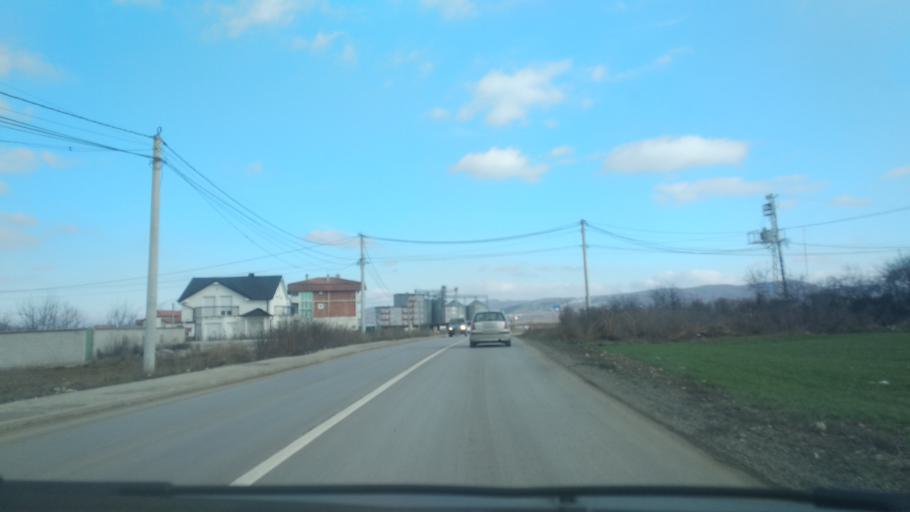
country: XK
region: Pristina
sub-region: Komuna e Obiliqit
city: Obiliq
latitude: 42.7290
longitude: 21.1000
